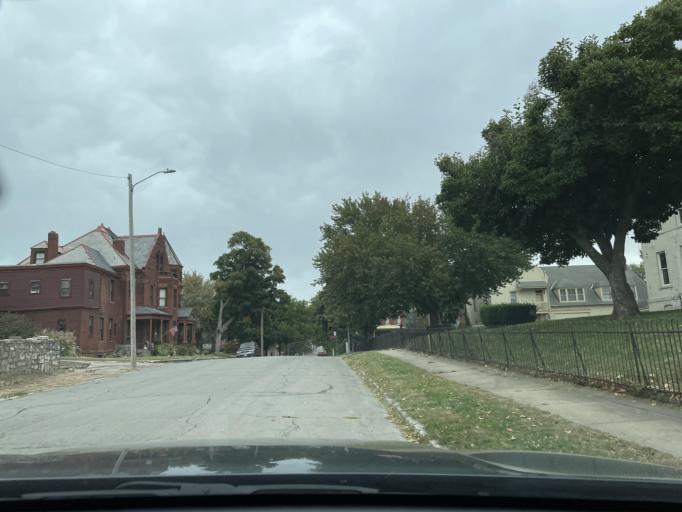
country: US
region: Missouri
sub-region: Buchanan County
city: Saint Joseph
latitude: 39.7650
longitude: -94.8463
